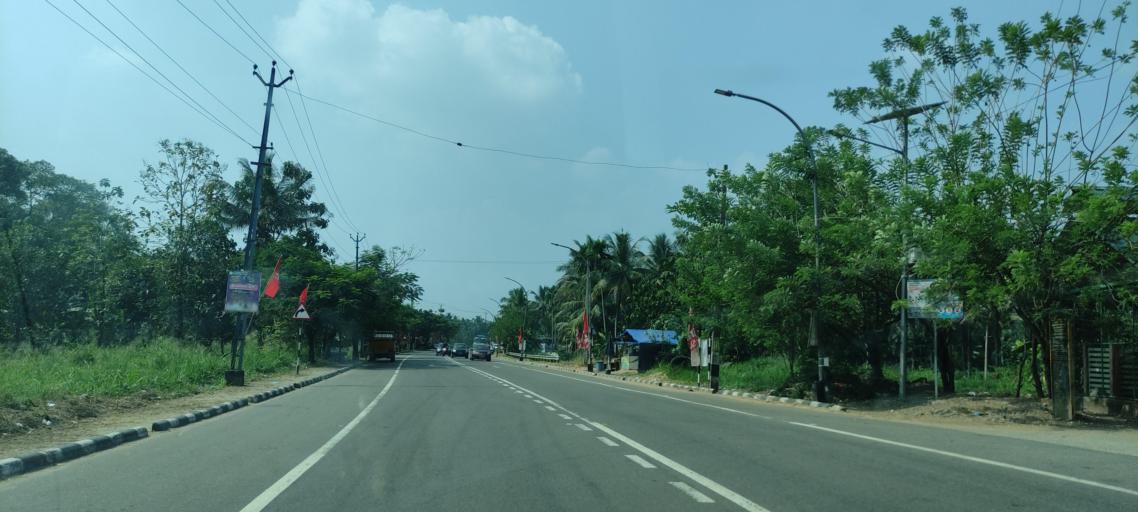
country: IN
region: Kerala
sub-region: Pattanamtitta
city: Adur
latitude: 9.1557
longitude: 76.7260
